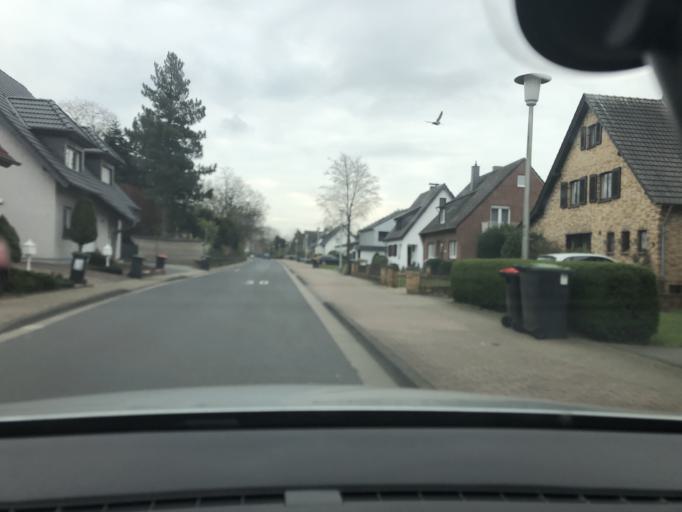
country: DE
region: North Rhine-Westphalia
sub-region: Regierungsbezirk Dusseldorf
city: Kamp-Lintfort
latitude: 51.4938
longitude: 6.5389
